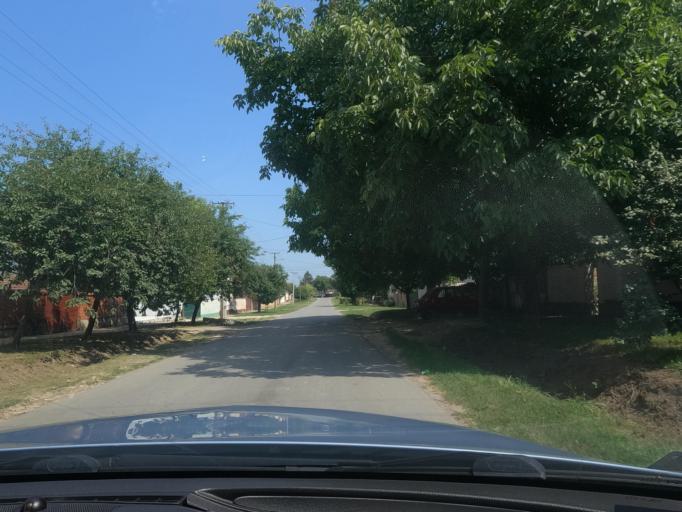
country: RS
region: Autonomna Pokrajina Vojvodina
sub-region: Juznobacki Okrug
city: Kovilj
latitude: 45.2211
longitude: 20.0331
